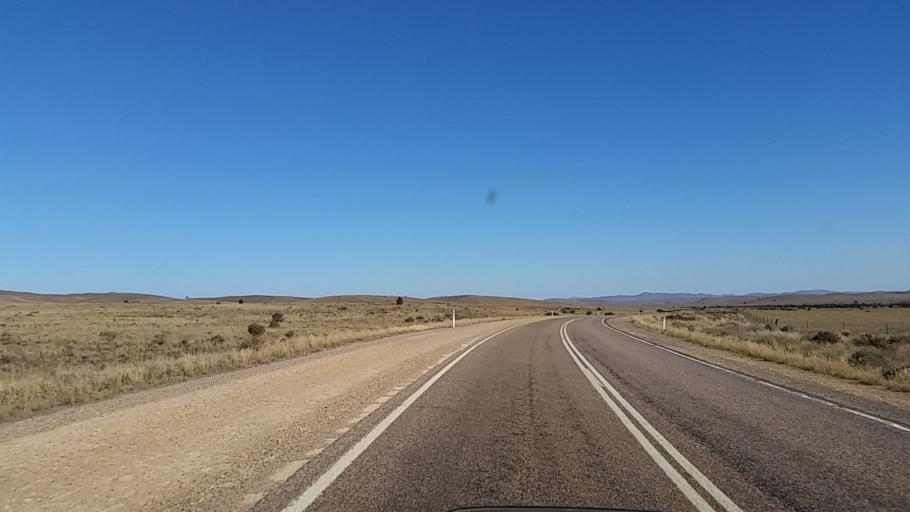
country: AU
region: South Australia
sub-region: Peterborough
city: Peterborough
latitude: -32.5658
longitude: 138.5645
